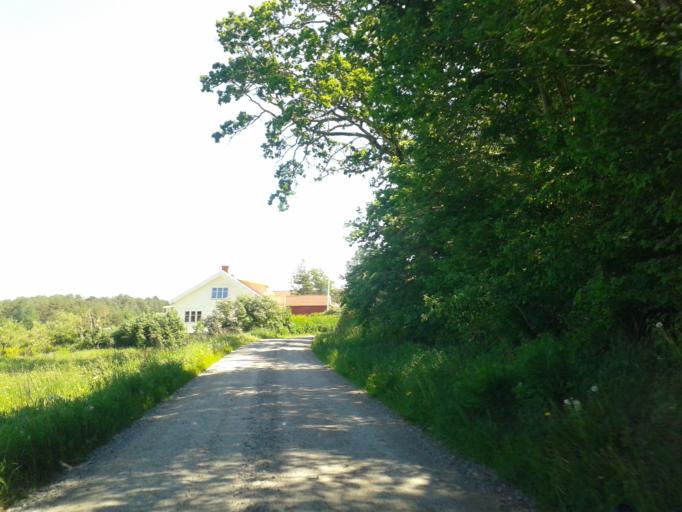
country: SE
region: Vaestra Goetaland
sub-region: Stromstads Kommun
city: Stroemstad
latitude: 58.8623
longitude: 11.2217
